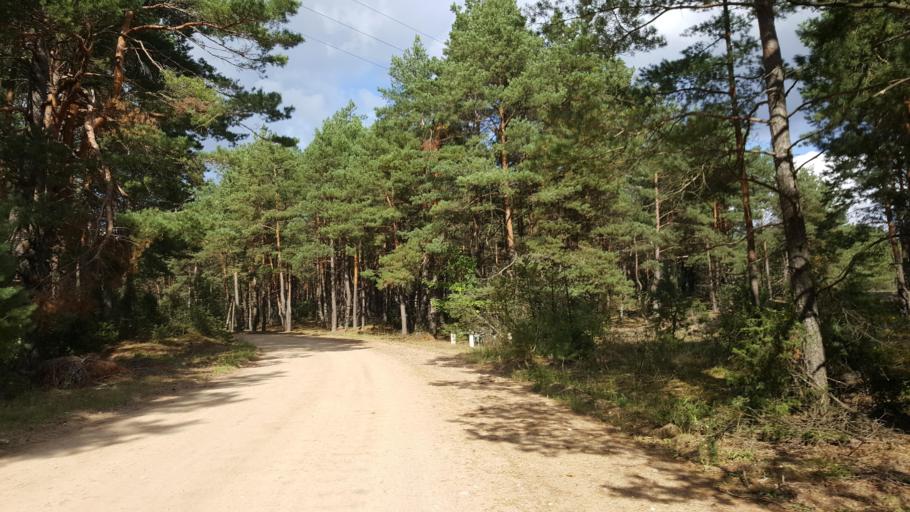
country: BY
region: Brest
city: Kamyanyets
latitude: 52.4340
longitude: 23.9440
